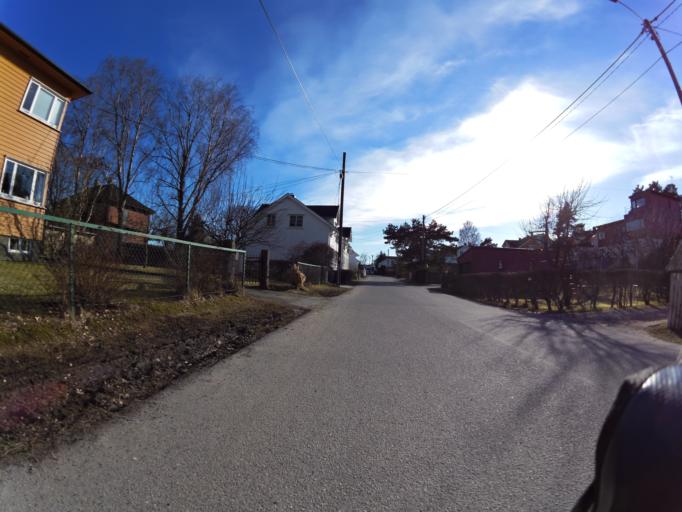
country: NO
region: Ostfold
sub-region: Fredrikstad
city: Fredrikstad
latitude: 59.2174
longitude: 10.9104
